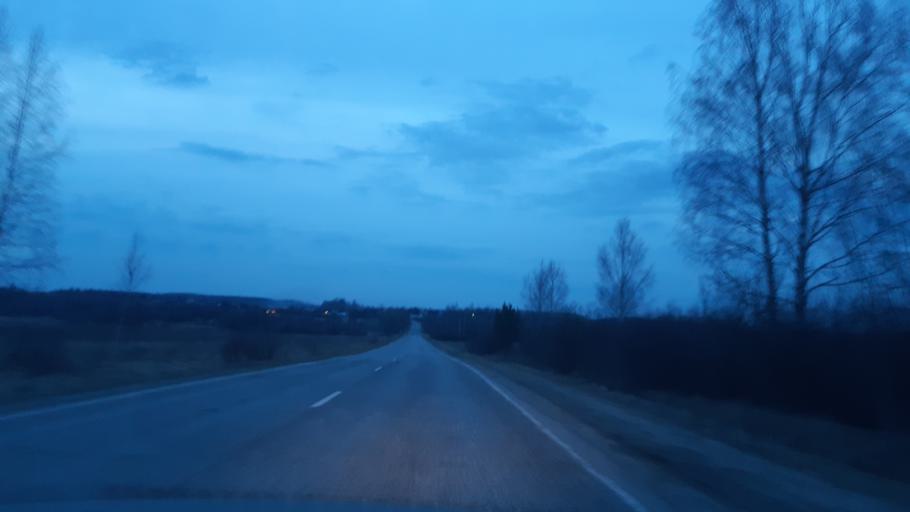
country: RU
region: Vladimir
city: Luknovo
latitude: 56.2081
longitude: 42.0327
